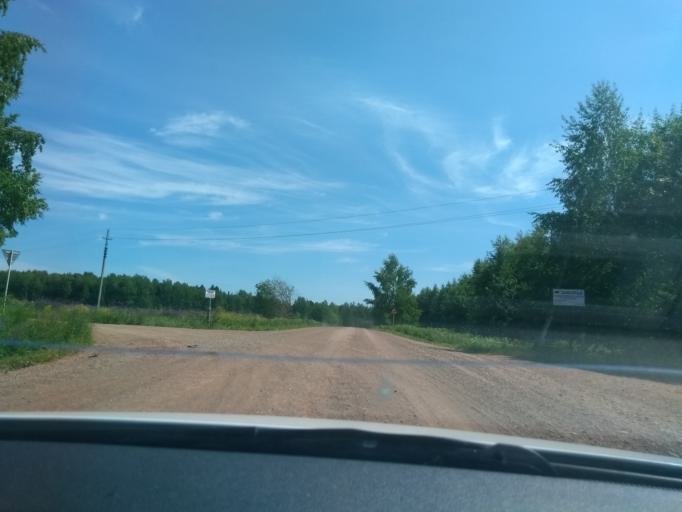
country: RU
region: Perm
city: Sylva
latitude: 57.8164
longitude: 56.7282
